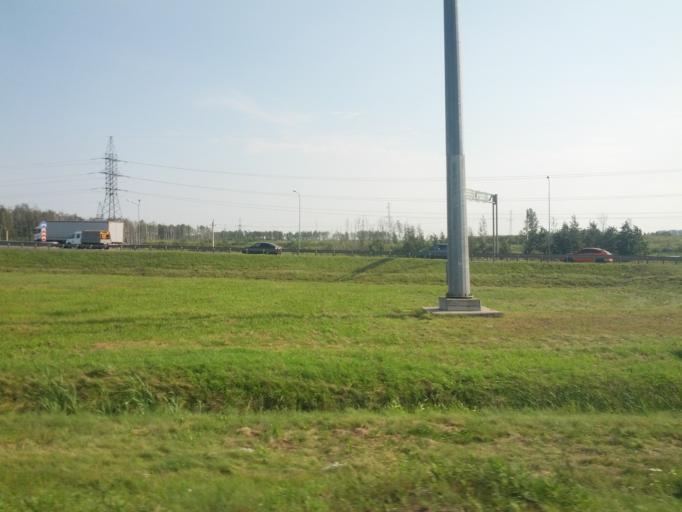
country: RU
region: Leningrad
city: Rybatskoye
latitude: 59.8902
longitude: 30.5162
